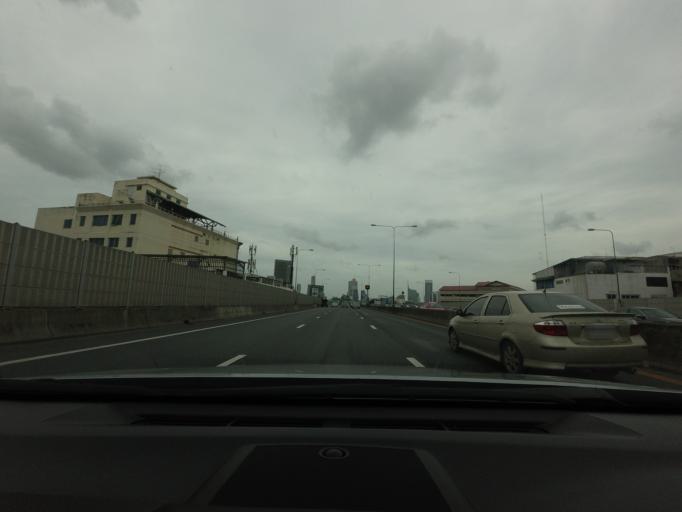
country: TH
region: Bangkok
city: Pathum Wan
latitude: 13.7434
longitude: 100.5203
